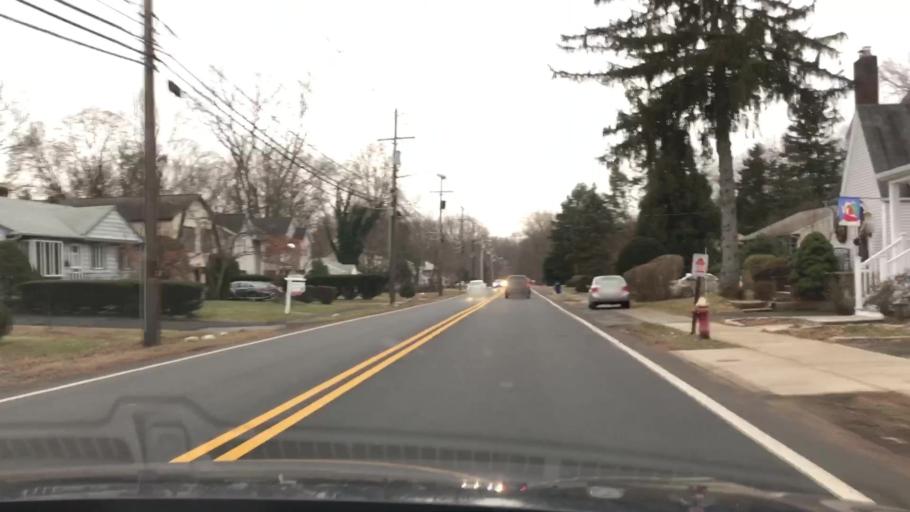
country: US
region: New Jersey
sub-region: Bergen County
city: Norwood
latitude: 40.9914
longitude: -73.9575
